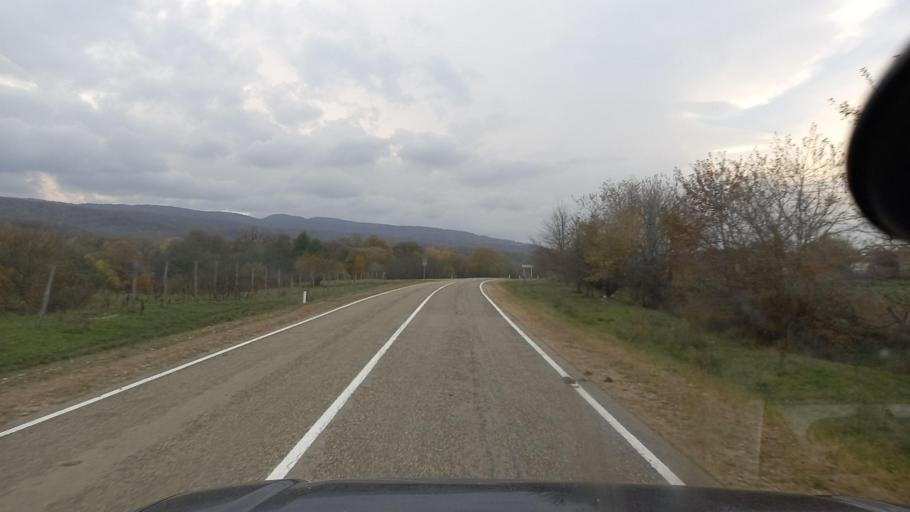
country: RU
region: Krasnodarskiy
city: Gubskaya
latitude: 44.2959
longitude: 40.5459
